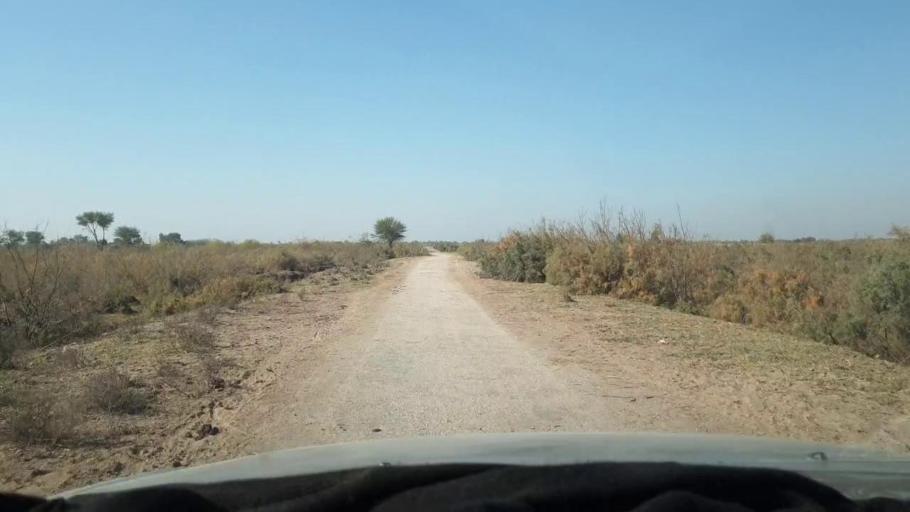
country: PK
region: Sindh
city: Adilpur
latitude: 27.8960
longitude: 69.2486
